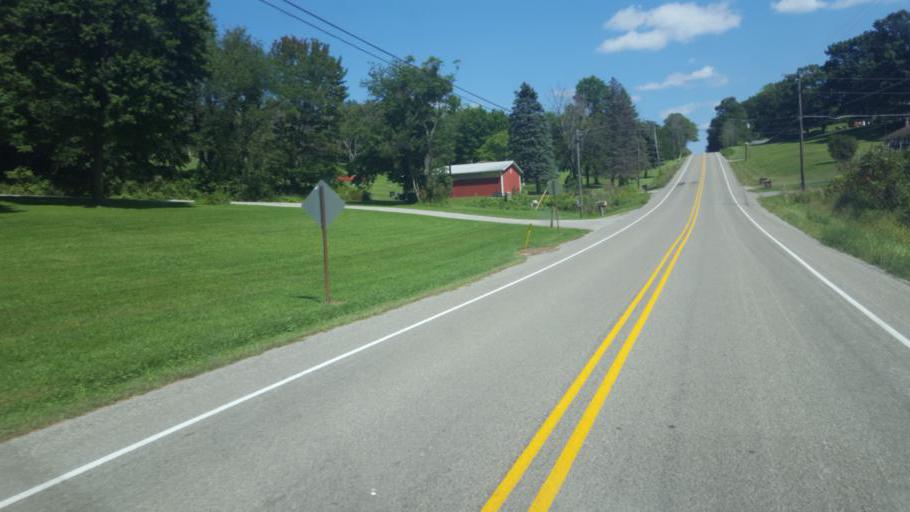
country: US
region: Pennsylvania
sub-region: Clarion County
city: Knox
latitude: 41.1095
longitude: -79.6129
